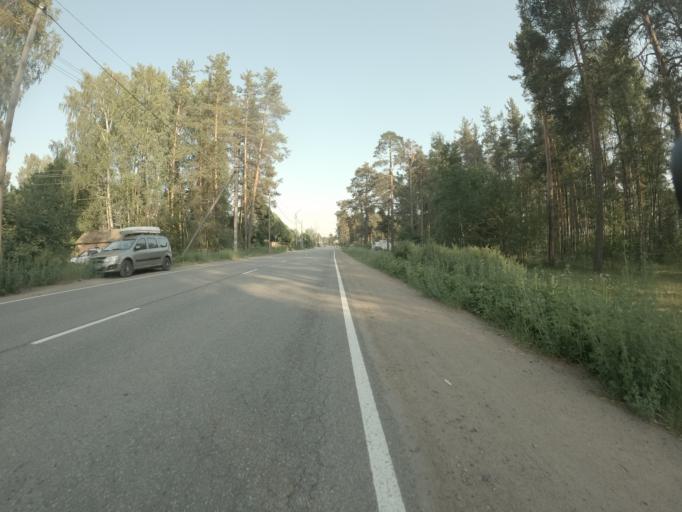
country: RU
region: Leningrad
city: Yakovlevo
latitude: 60.4709
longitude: 29.2833
